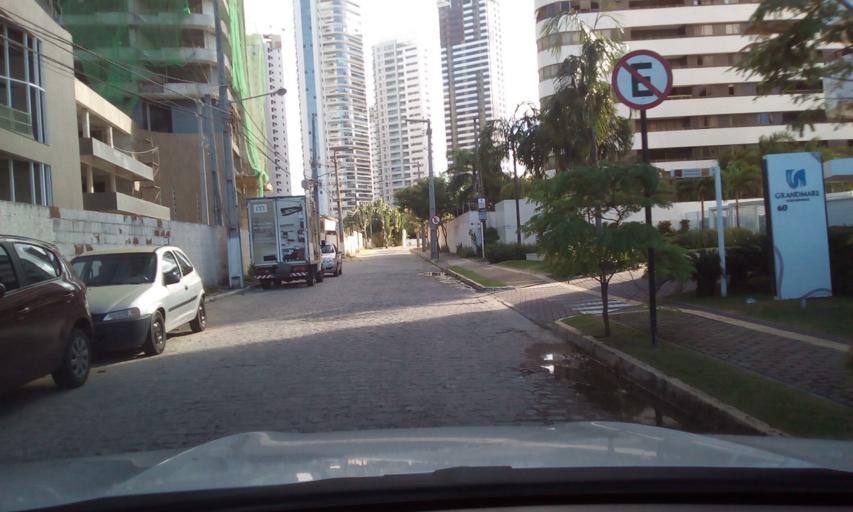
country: BR
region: Paraiba
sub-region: Joao Pessoa
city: Joao Pessoa
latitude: -7.1298
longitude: -34.8272
